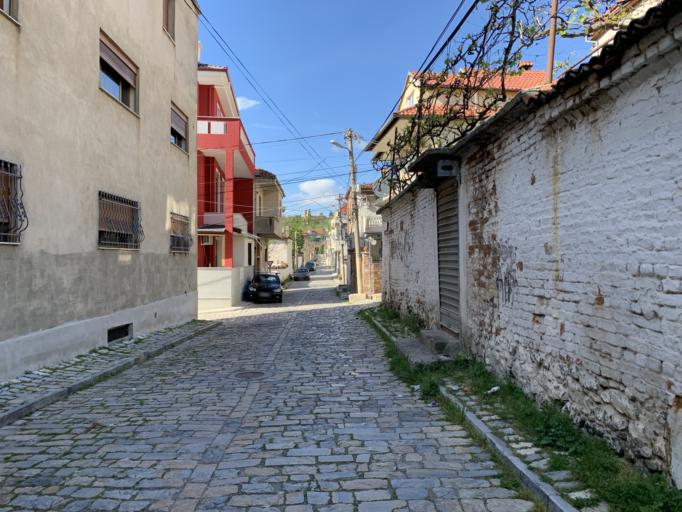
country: AL
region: Korce
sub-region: Rrethi i Korces
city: Korce
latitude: 40.6195
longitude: 20.7851
